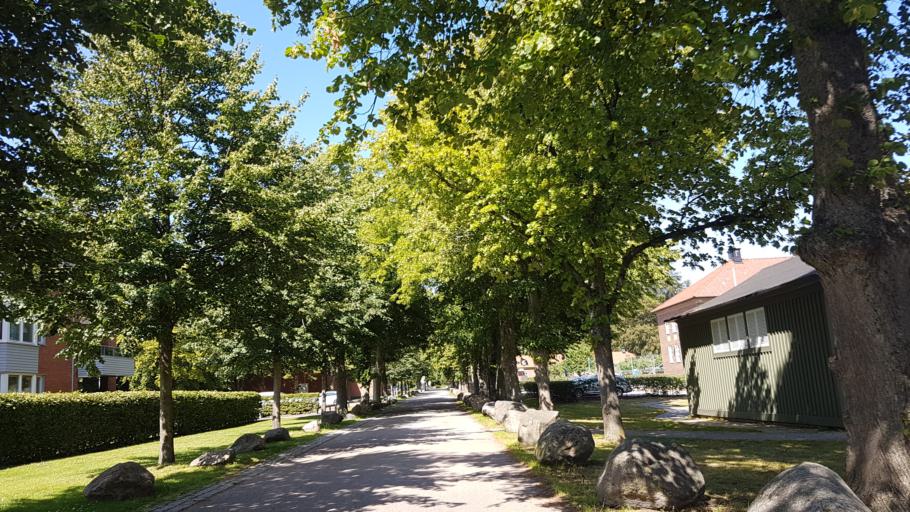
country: SE
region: Skane
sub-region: Helsingborg
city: Helsingborg
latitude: 56.0804
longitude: 12.6832
